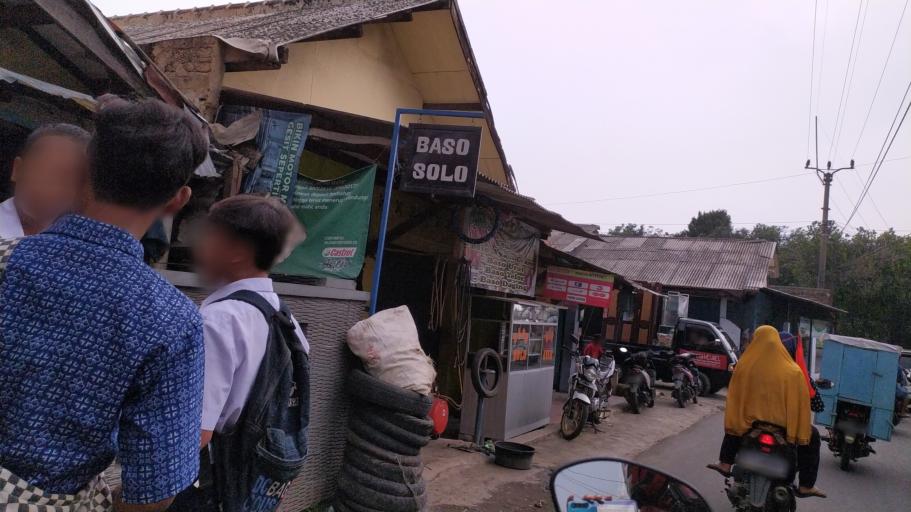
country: ID
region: West Java
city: Ciampea
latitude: -6.6036
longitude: 106.7020
